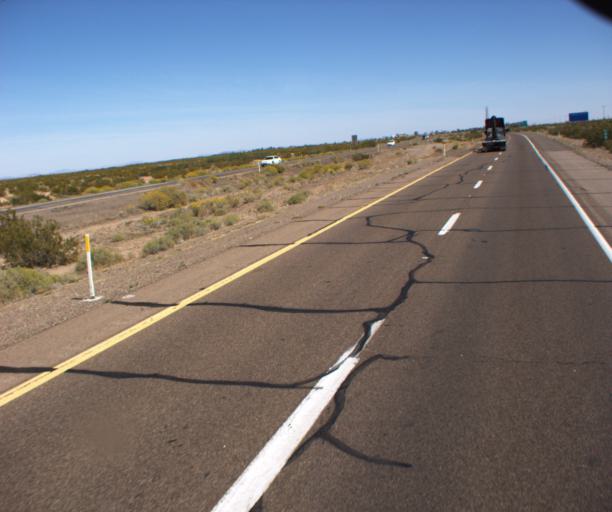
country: US
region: Arizona
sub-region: Yuma County
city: Wellton
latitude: 32.7885
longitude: -113.5619
